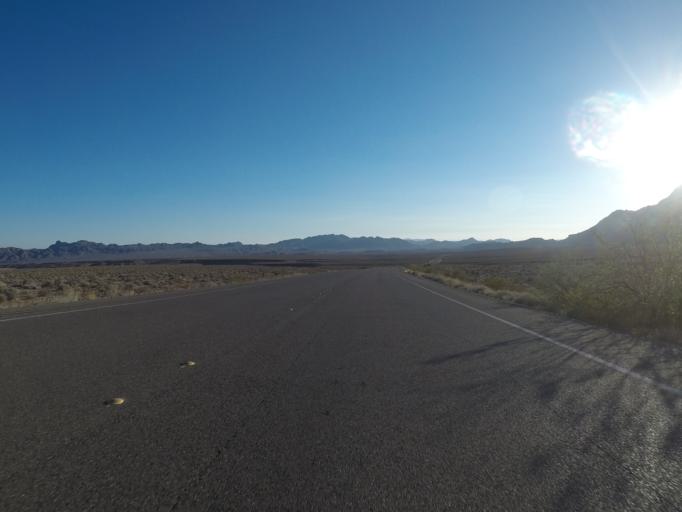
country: US
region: Nevada
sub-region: Clark County
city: Moapa Valley
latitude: 36.3489
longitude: -114.4841
